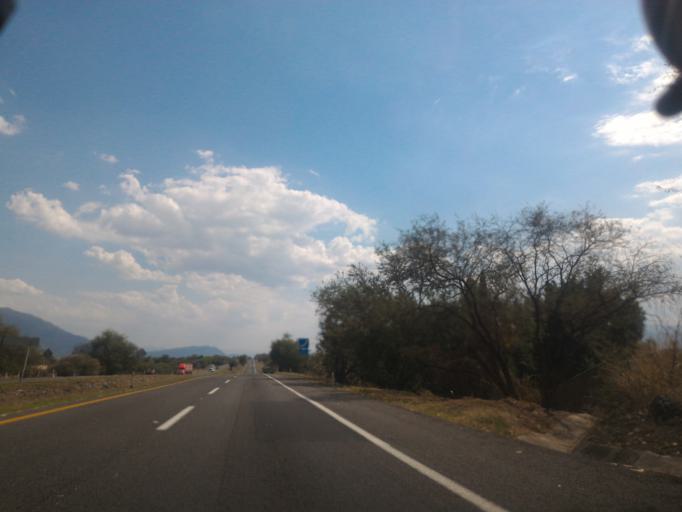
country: MX
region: Jalisco
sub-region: Acatlan de Juarez
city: Villa de los Ninos
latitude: 20.3503
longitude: -103.5754
